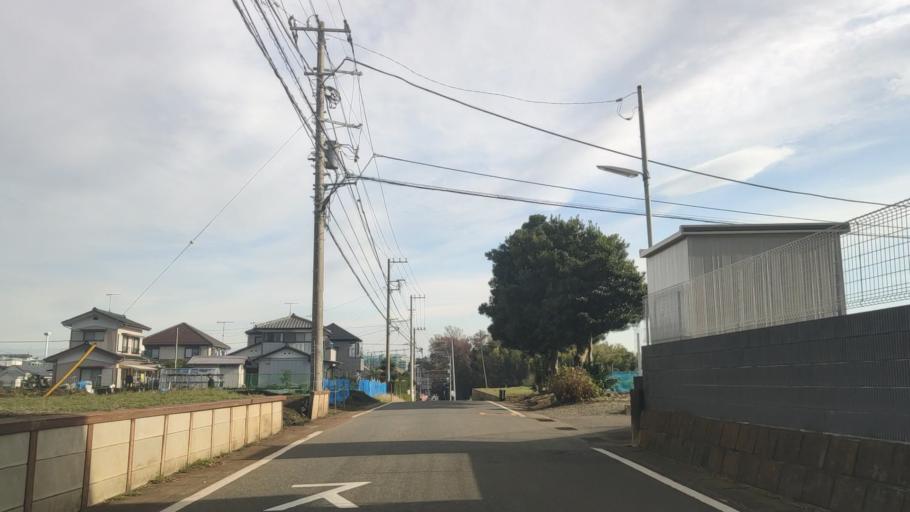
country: JP
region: Kanagawa
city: Atsugi
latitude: 35.4314
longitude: 139.3935
